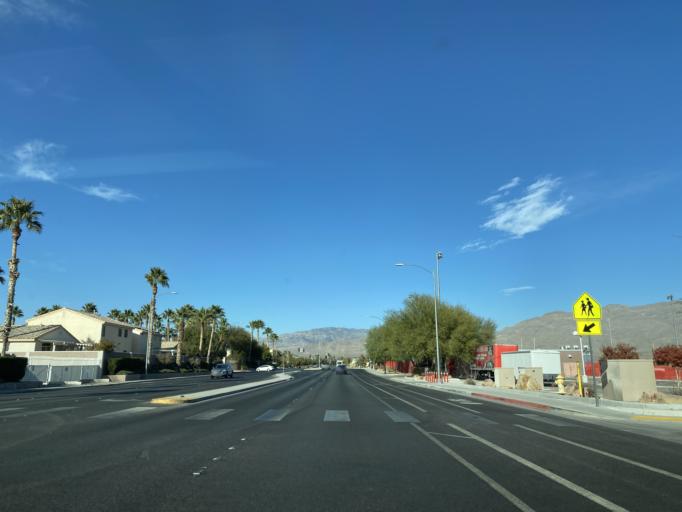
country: US
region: Nevada
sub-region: Clark County
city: North Las Vegas
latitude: 36.3024
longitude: -115.2601
